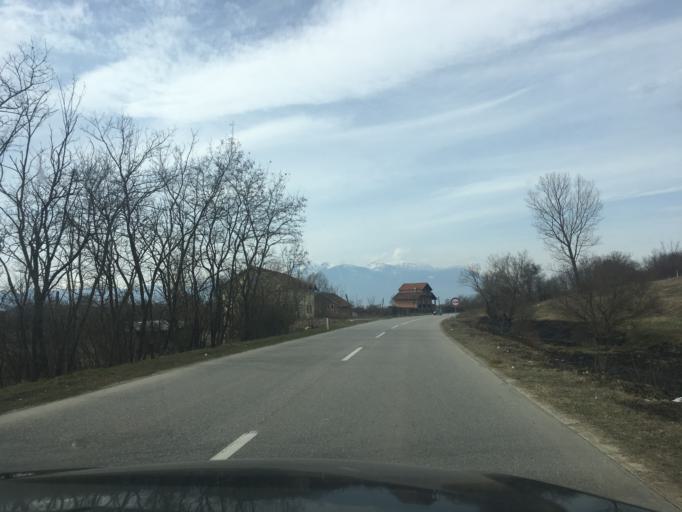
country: XK
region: Pec
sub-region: Komuna e Pejes
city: Kosuriq
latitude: 42.6204
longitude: 20.4811
